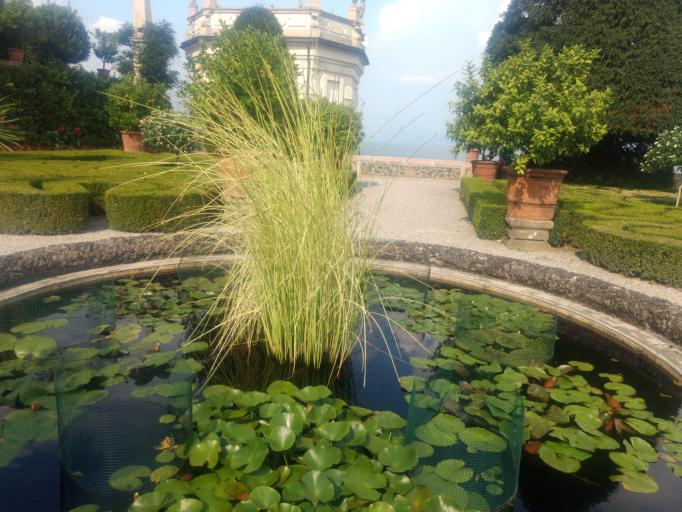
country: IT
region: Piedmont
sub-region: Provincia Verbano-Cusio-Ossola
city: Stresa
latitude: 45.8943
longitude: 8.5281
